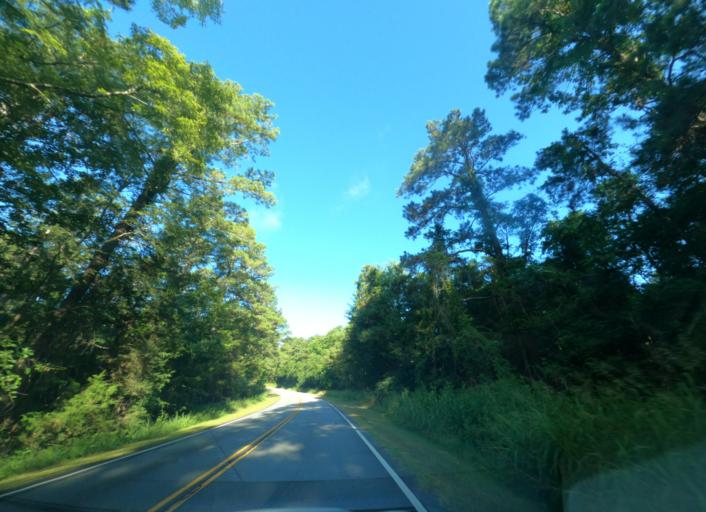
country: US
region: South Carolina
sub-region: McCormick County
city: McCormick
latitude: 33.8891
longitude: -82.4022
